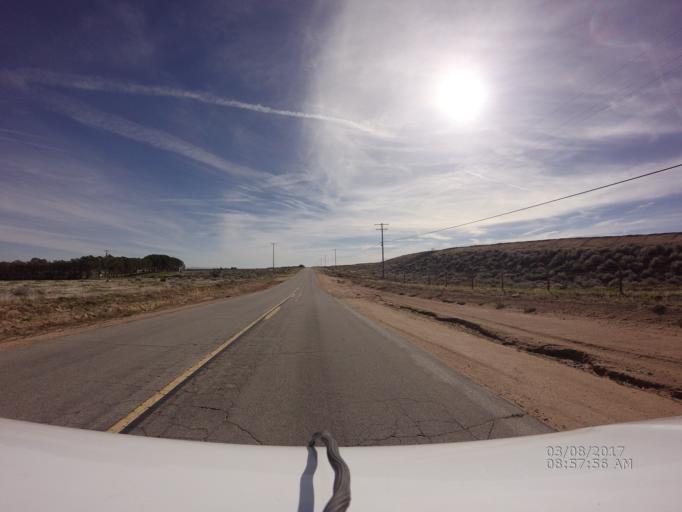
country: US
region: California
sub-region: Los Angeles County
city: Green Valley
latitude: 34.7610
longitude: -118.5411
